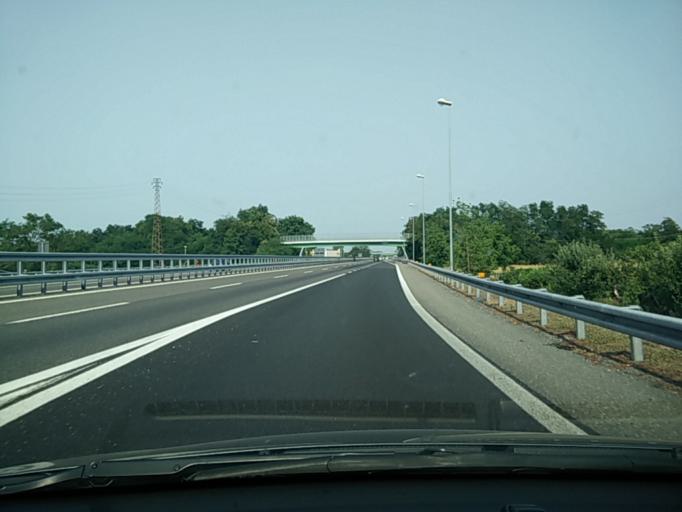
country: IT
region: Lombardy
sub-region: Provincia di Pavia
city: Stradella
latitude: 45.0801
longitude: 9.2795
